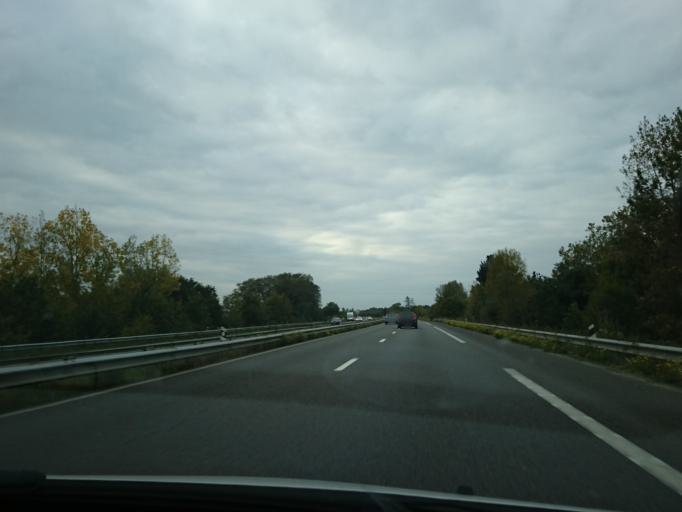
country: FR
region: Pays de la Loire
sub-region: Departement de la Loire-Atlantique
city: Pontchateau
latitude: 47.4463
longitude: -2.0883
